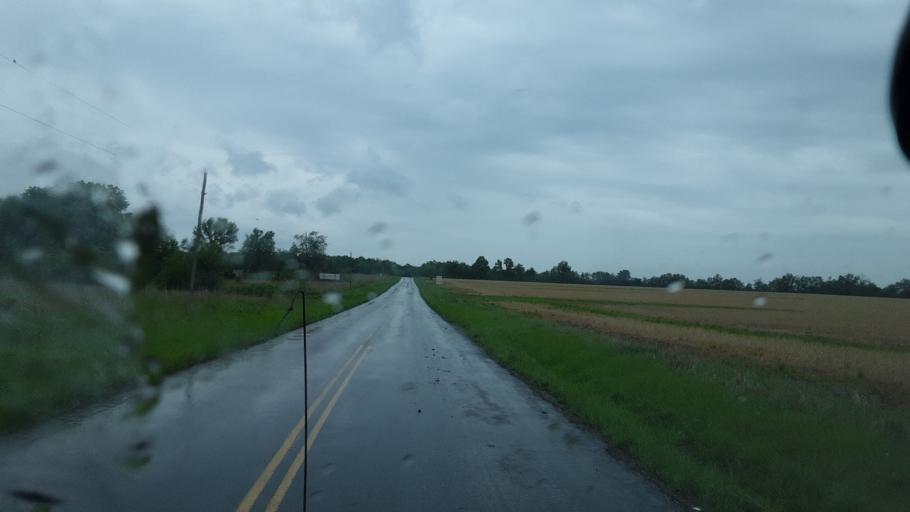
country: US
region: Missouri
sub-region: Randolph County
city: Moberly
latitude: 39.3925
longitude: -92.2484
